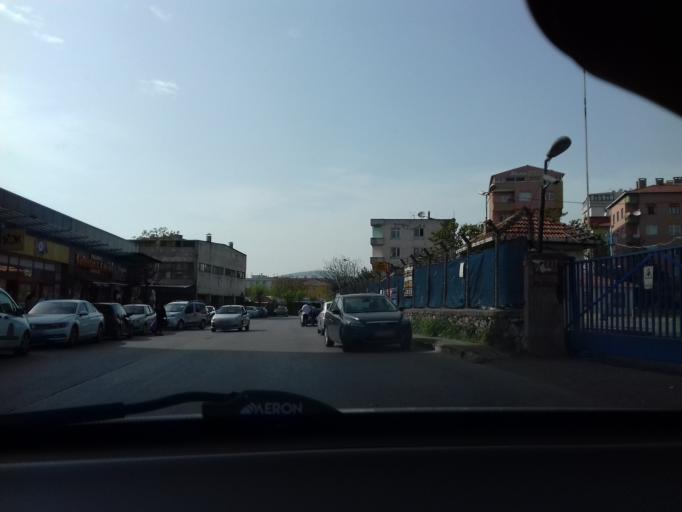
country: TR
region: Istanbul
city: Maltepe
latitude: 40.9138
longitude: 29.2089
